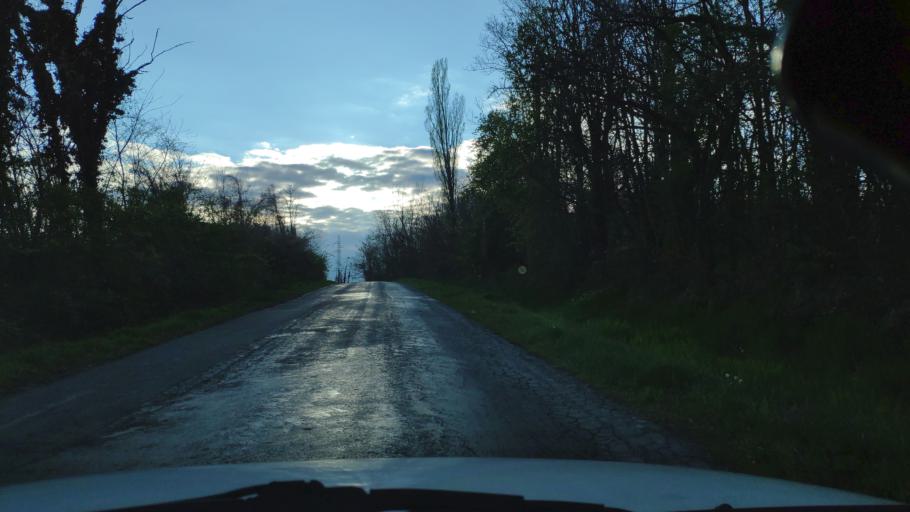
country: HU
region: Zala
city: Nagykanizsa
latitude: 46.4204
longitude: 17.1011
